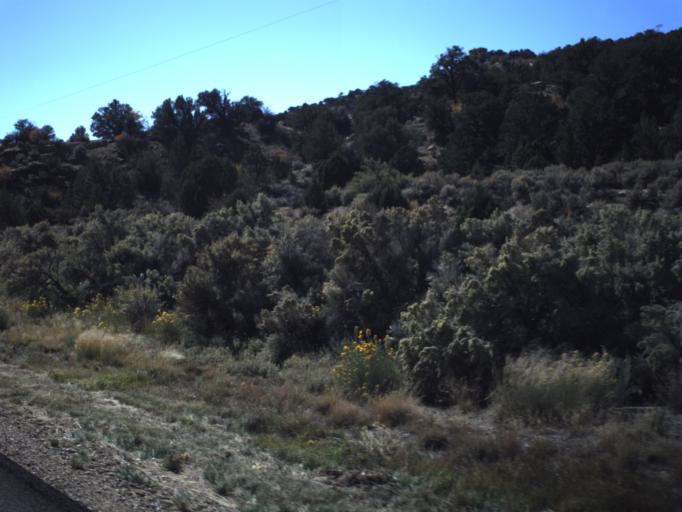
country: US
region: Utah
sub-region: Garfield County
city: Panguitch
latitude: 37.6011
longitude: -111.9175
